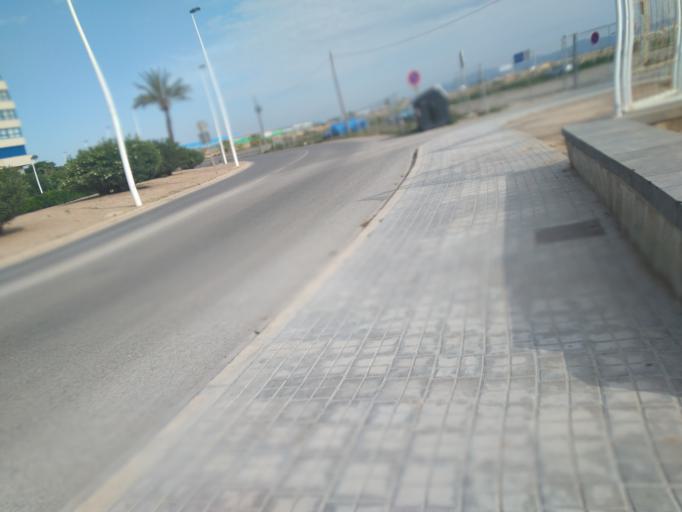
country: ES
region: Valencia
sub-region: Provincia de Valencia
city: Alboraya
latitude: 39.4944
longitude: -0.3254
